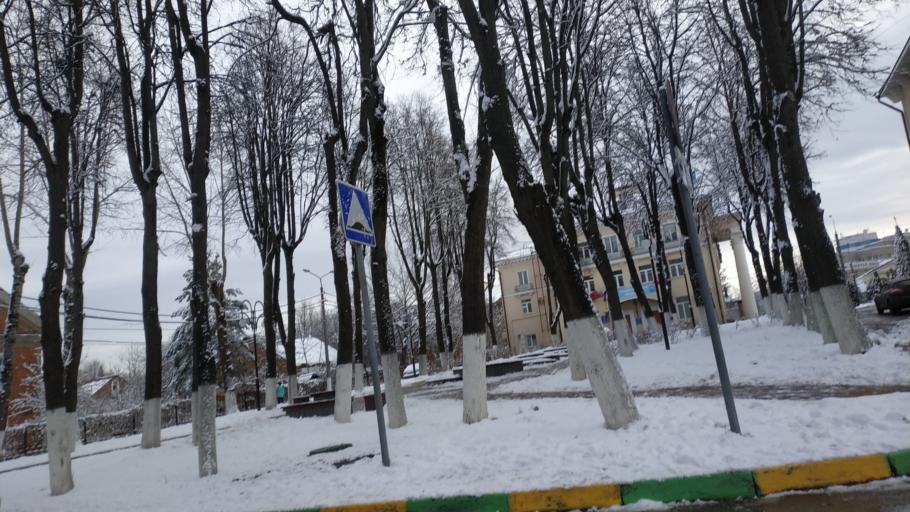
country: RU
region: Moskovskaya
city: Vidnoye
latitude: 55.5579
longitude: 37.7085
